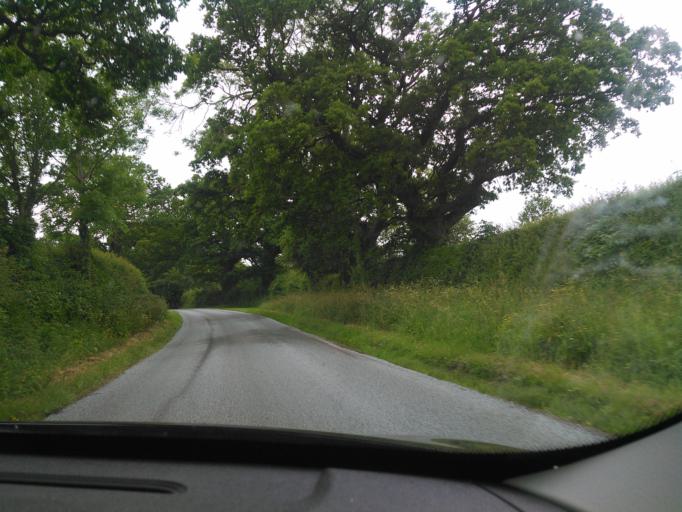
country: GB
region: England
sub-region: Shropshire
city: Wem
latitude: 52.8895
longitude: -2.7531
